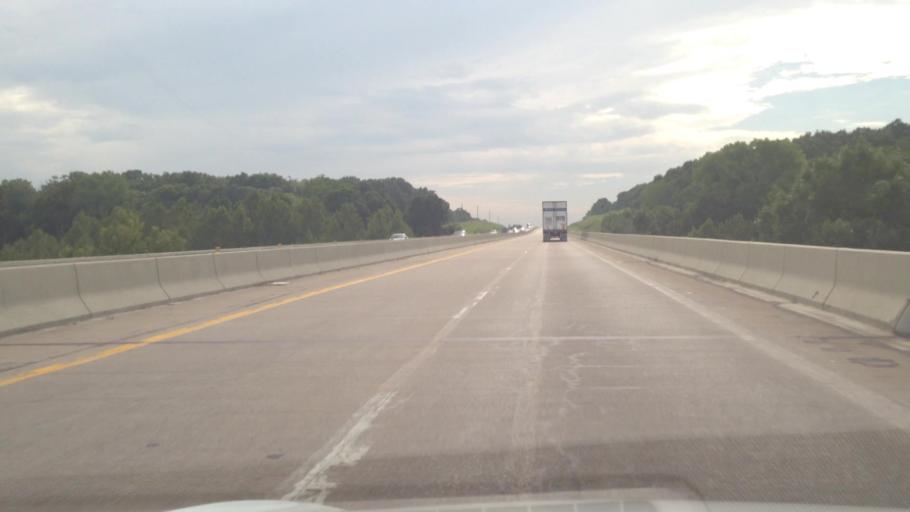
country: US
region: Kansas
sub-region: Cherokee County
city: Baxter Springs
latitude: 36.9263
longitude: -94.7403
